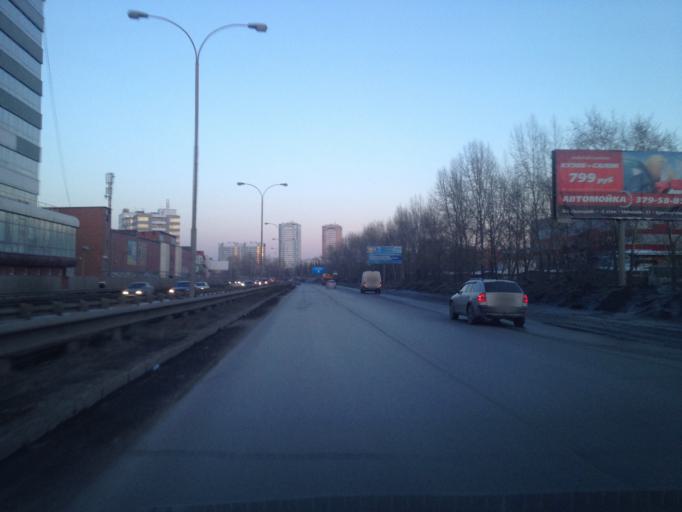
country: RU
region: Sverdlovsk
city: Yekaterinburg
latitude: 56.7877
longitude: 60.6240
